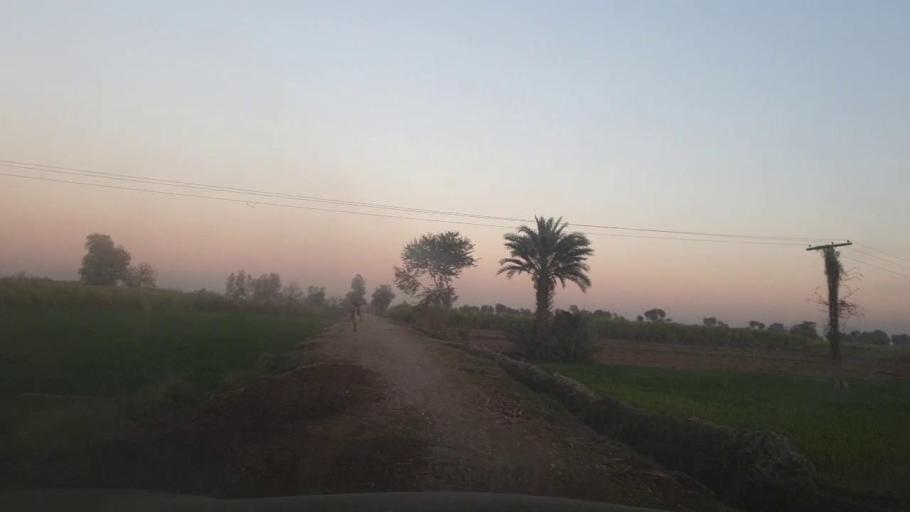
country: PK
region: Sindh
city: Ghotki
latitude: 28.0223
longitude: 69.3847
